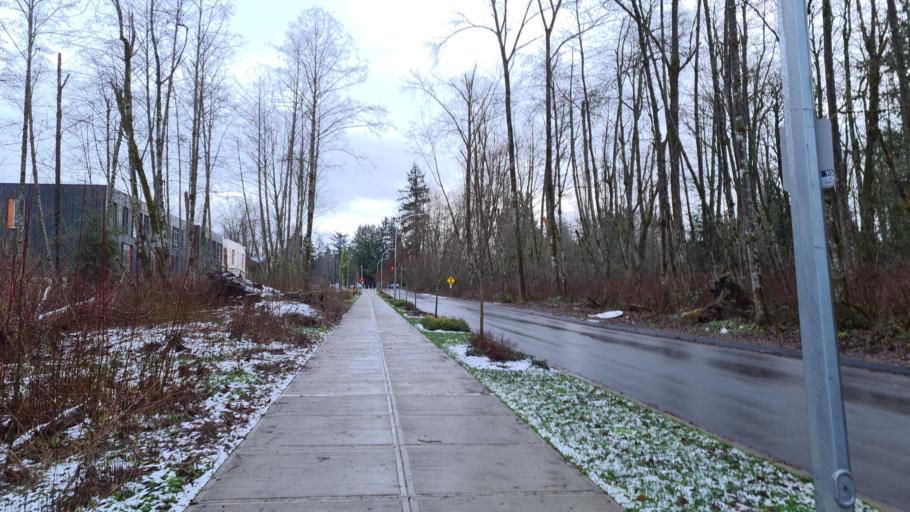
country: CA
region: British Columbia
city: Walnut Grove
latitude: 49.1410
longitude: -122.6647
